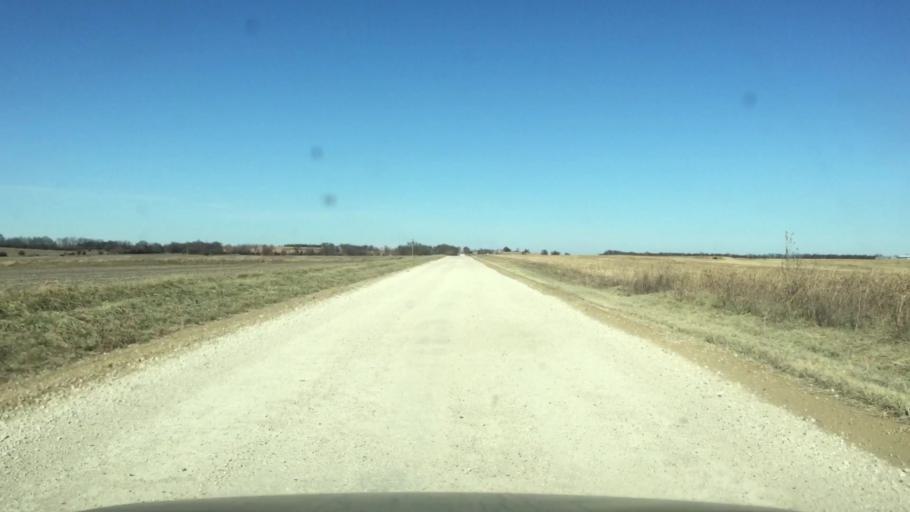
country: US
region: Kansas
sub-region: Allen County
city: Iola
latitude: 37.8604
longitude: -95.3910
